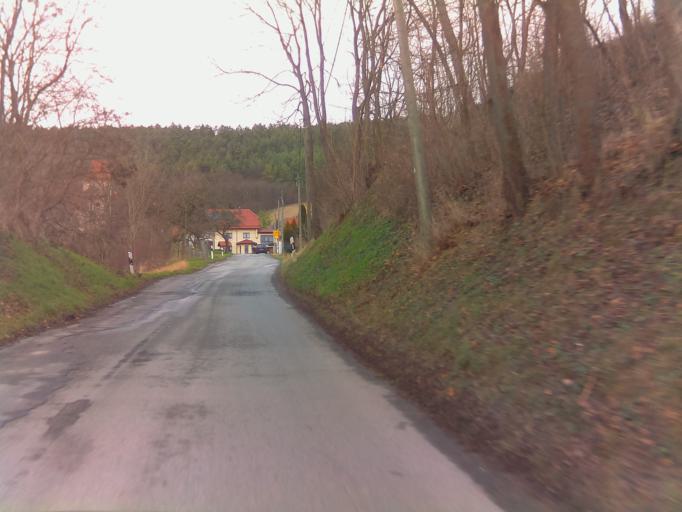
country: DE
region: Thuringia
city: Bibra
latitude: 50.8117
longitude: 11.5485
